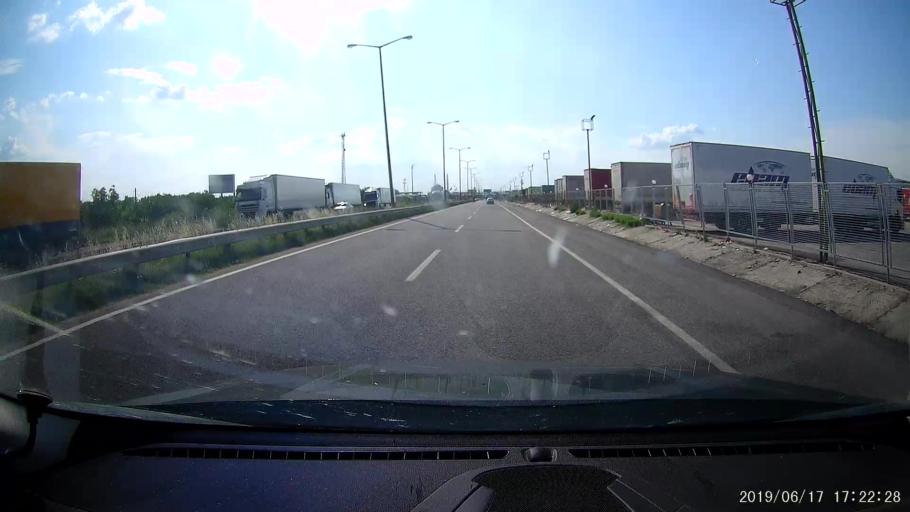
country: GR
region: East Macedonia and Thrace
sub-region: Nomos Evrou
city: Rizia
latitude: 41.7119
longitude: 26.3741
